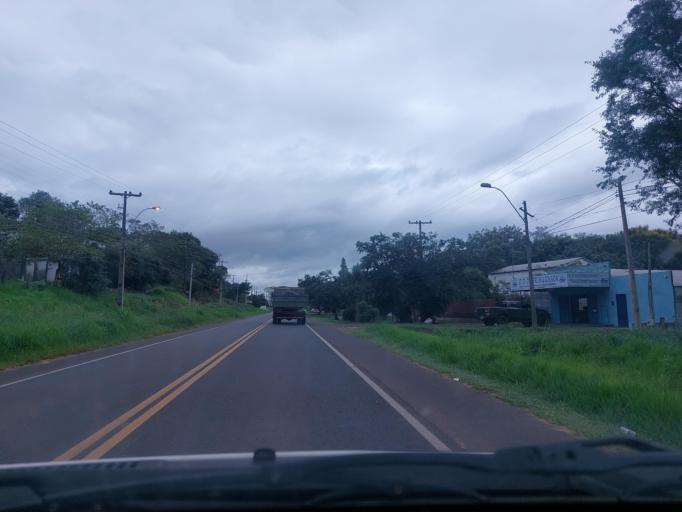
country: PY
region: San Pedro
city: Guayaybi
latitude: -24.6647
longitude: -56.4152
